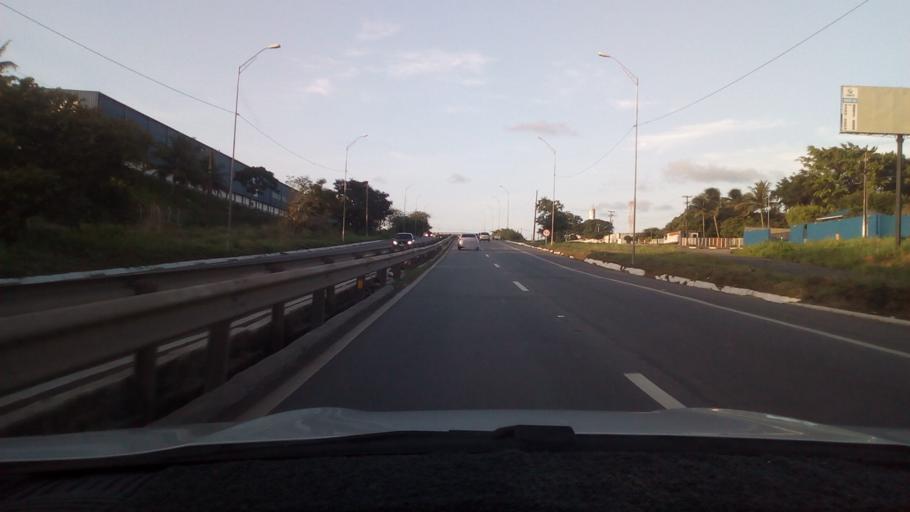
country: BR
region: Paraiba
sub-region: Bayeux
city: Bayeux
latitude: -7.1866
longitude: -34.9024
